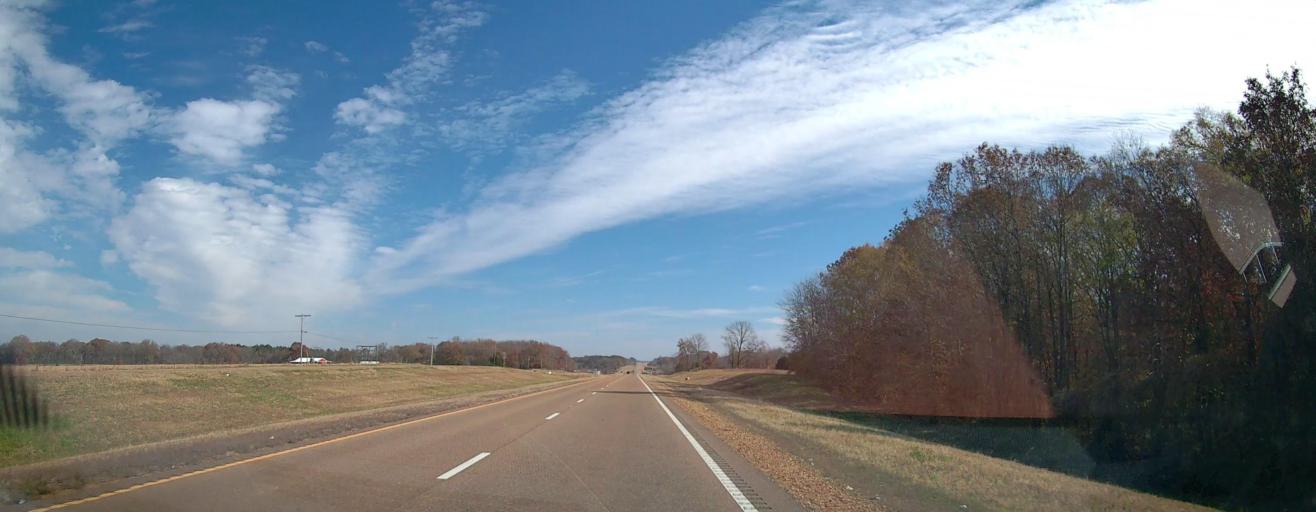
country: US
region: Mississippi
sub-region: Benton County
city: Ashland
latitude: 34.9461
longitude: -89.3074
